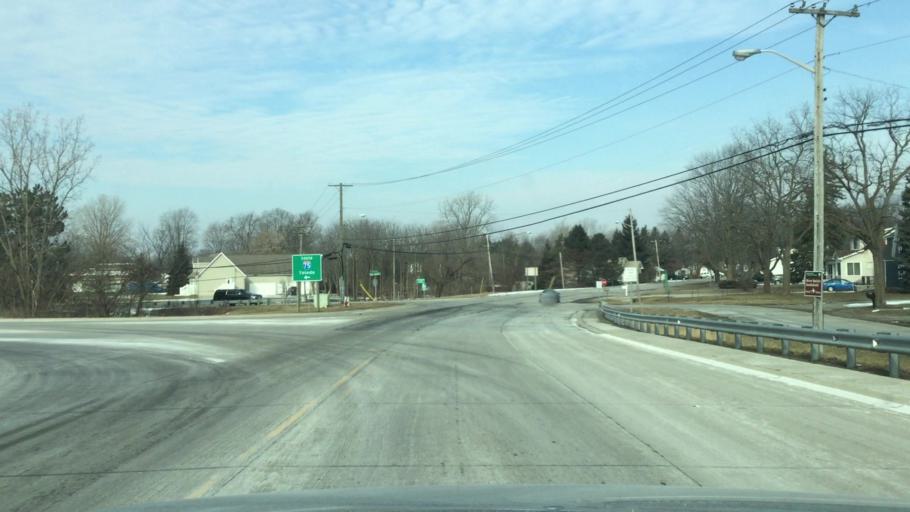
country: US
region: Michigan
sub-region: Monroe County
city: South Rockwood
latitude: 42.0632
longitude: -83.2601
